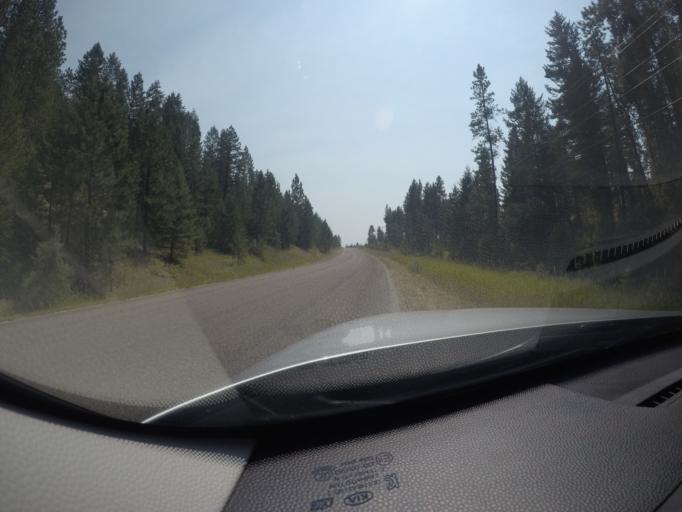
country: US
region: Montana
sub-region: Lake County
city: Polson
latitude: 47.7679
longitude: -114.1680
